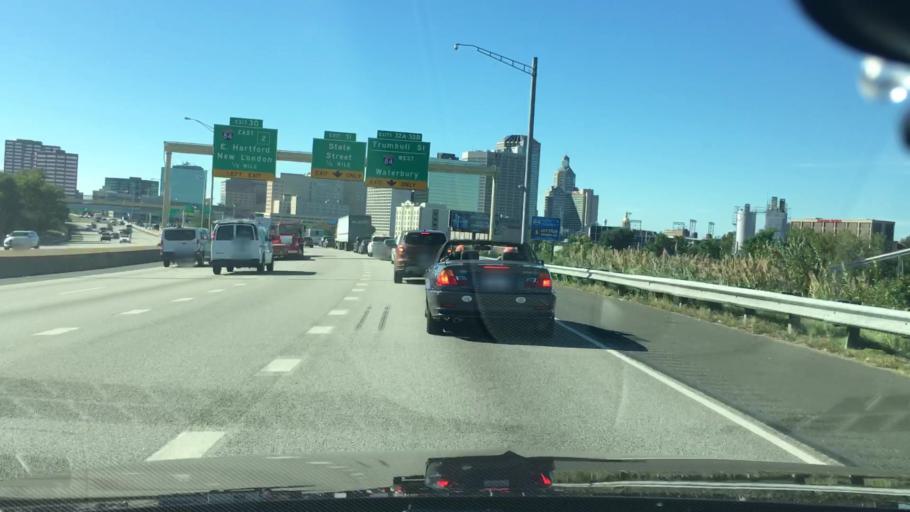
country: US
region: Connecticut
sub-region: Hartford County
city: Hartford
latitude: 41.7770
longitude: -72.6676
